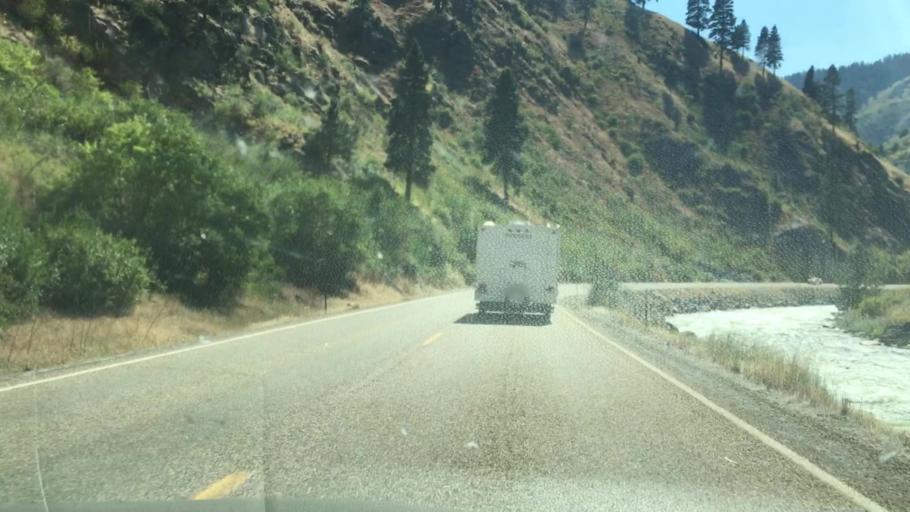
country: US
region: Idaho
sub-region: Boise County
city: Idaho City
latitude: 44.0904
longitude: -116.1053
